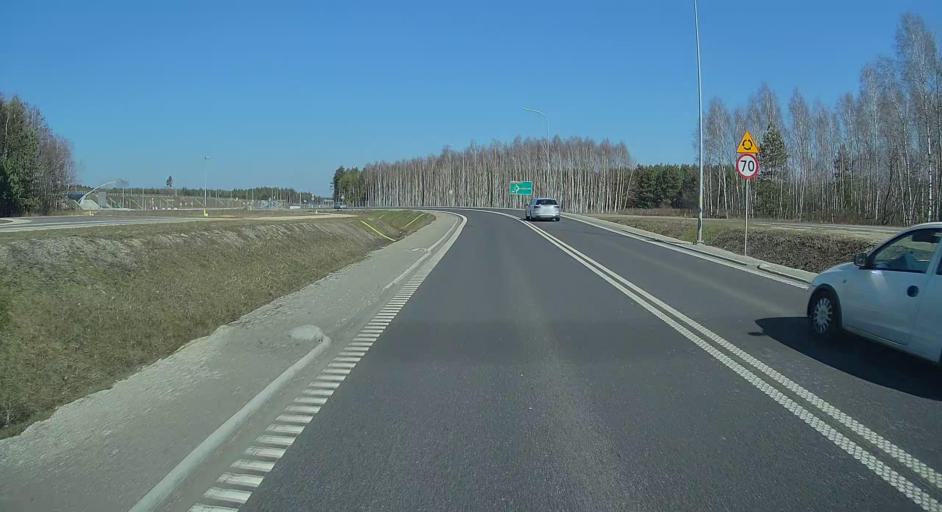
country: PL
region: Subcarpathian Voivodeship
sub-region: Powiat nizanski
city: Jarocin
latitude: 50.5717
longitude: 22.2520
